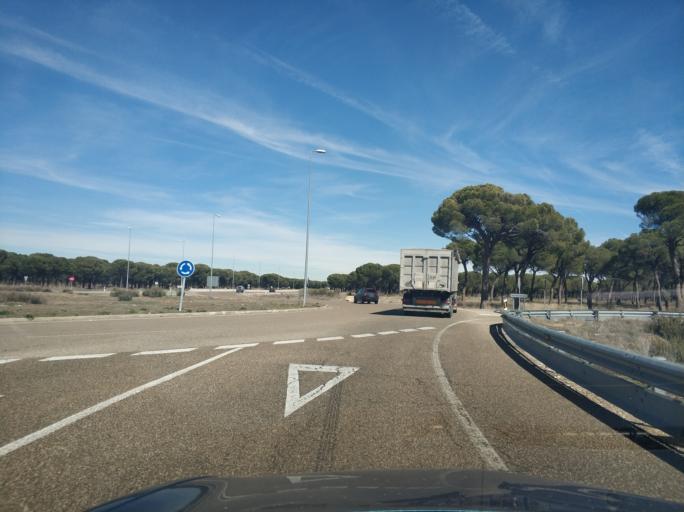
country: ES
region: Castille and Leon
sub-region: Provincia de Valladolid
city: Viana de Cega
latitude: 41.5615
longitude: -4.7865
